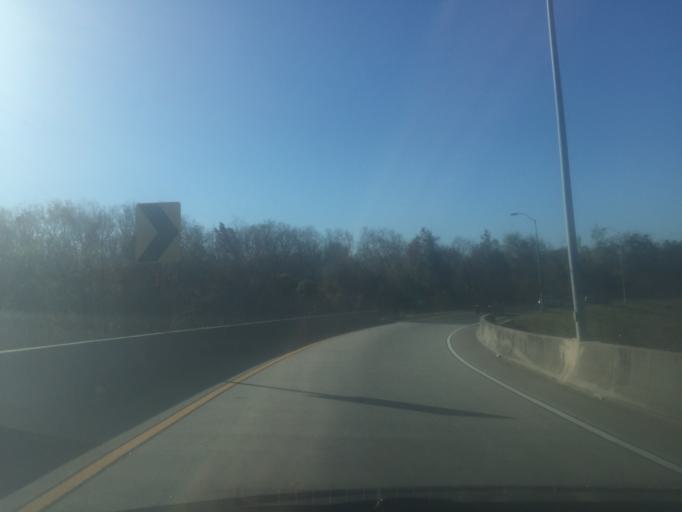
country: US
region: Georgia
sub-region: Chatham County
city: Savannah
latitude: 32.0803
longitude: -81.1065
